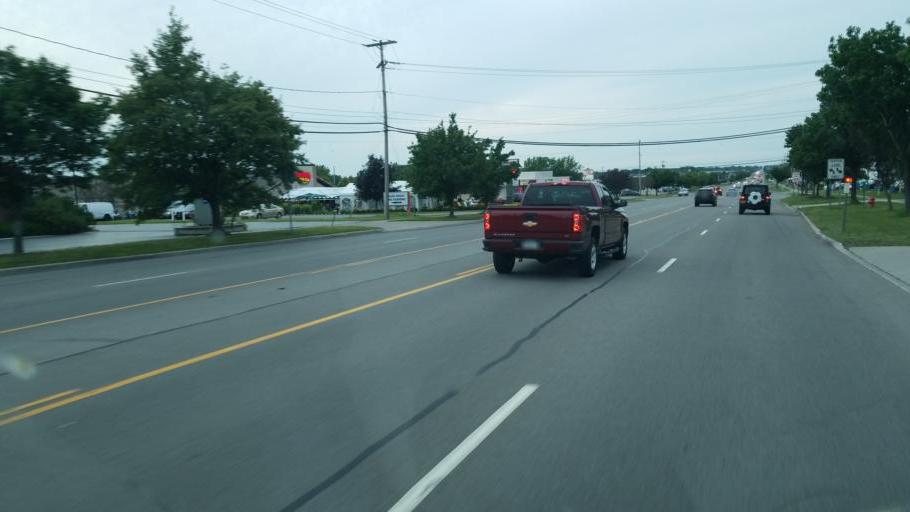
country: US
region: New York
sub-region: Erie County
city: Harris Hill
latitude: 42.9798
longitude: -78.6968
